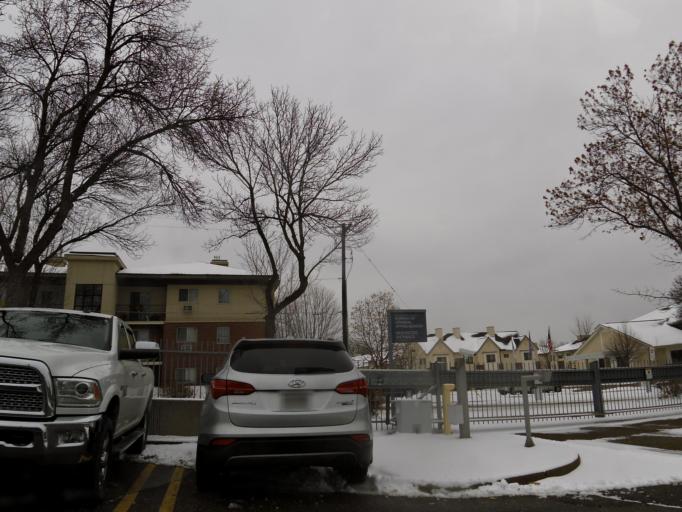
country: US
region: Minnesota
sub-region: Ramsey County
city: Maplewood
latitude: 44.9759
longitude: -93.0387
